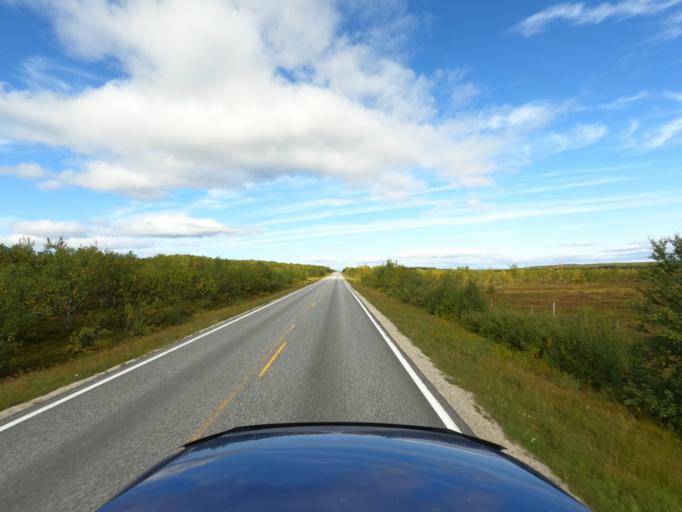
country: NO
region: Finnmark Fylke
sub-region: Karasjok
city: Karasjohka
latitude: 69.6488
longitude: 25.2803
